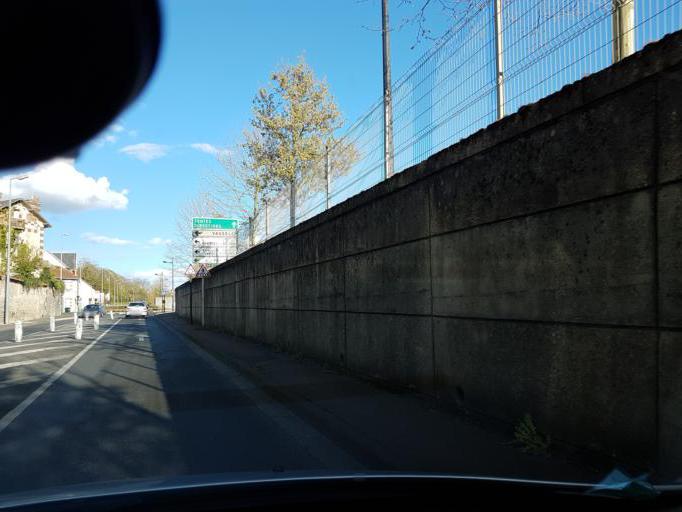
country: FR
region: Centre
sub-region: Departement du Cher
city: Bourges
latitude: 47.0954
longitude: 2.3938
